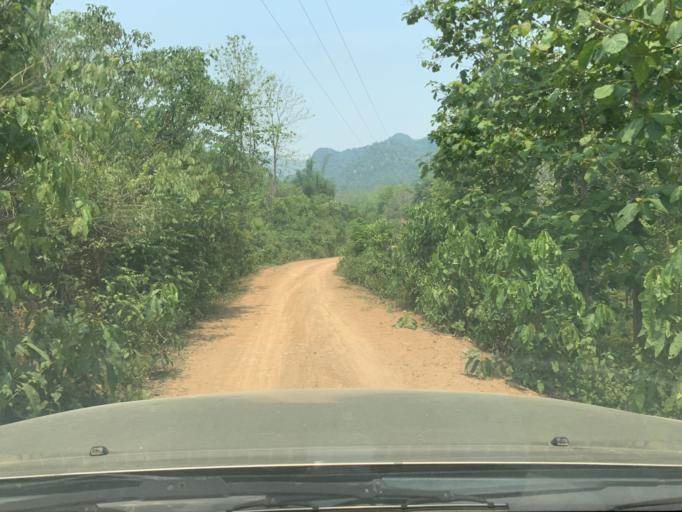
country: LA
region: Louangphabang
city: Louangphabang
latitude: 19.9658
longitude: 102.1269
